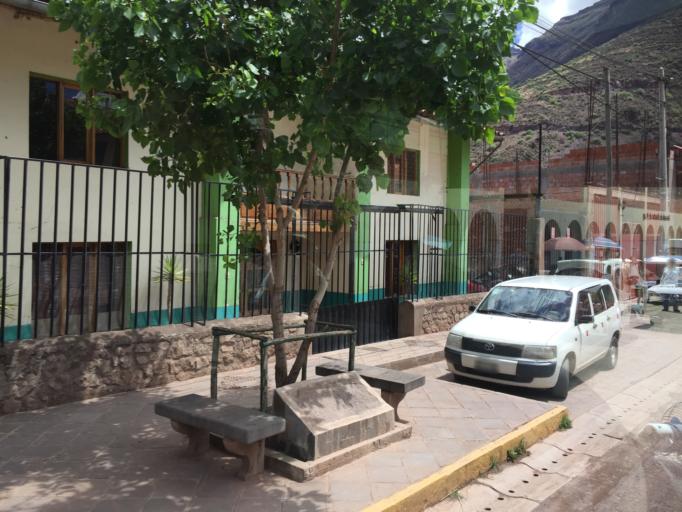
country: PE
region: Cusco
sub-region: Provincia de Calca
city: Pisac
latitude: -13.4216
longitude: -71.8486
